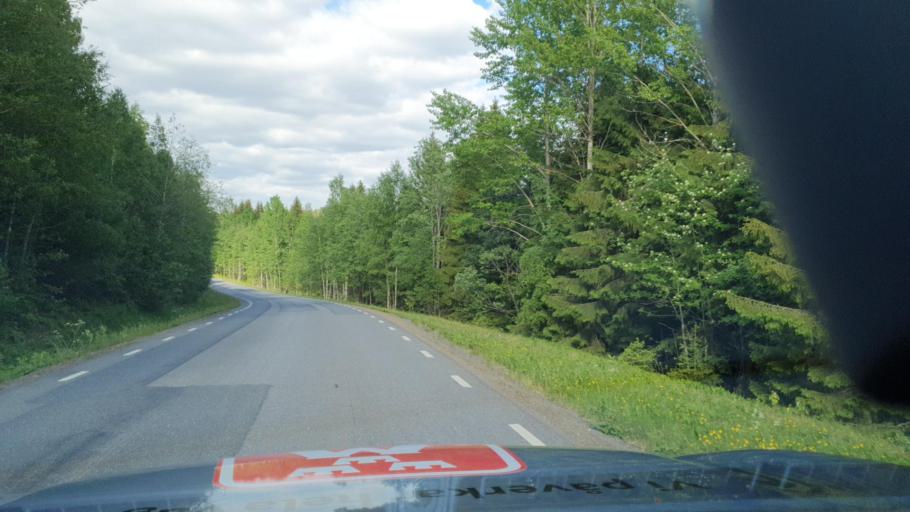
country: SE
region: Vaesternorrland
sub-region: Kramfors Kommun
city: Nordingra
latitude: 62.8184
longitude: 18.1708
